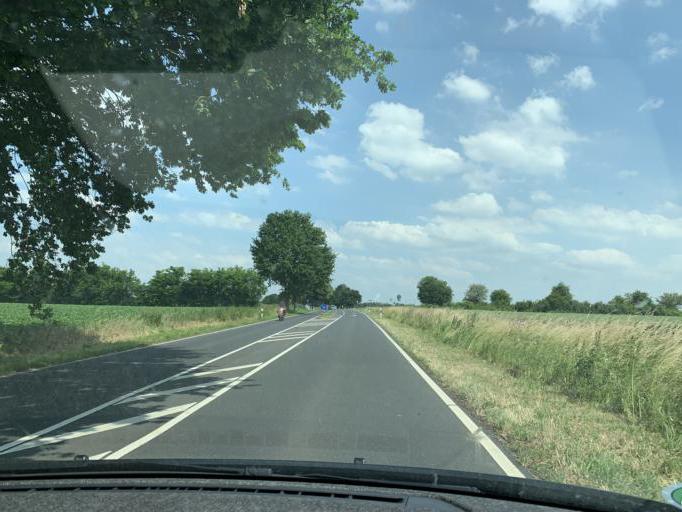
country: DE
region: North Rhine-Westphalia
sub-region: Regierungsbezirk Koln
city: Bedburg
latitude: 50.9814
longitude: 6.5443
